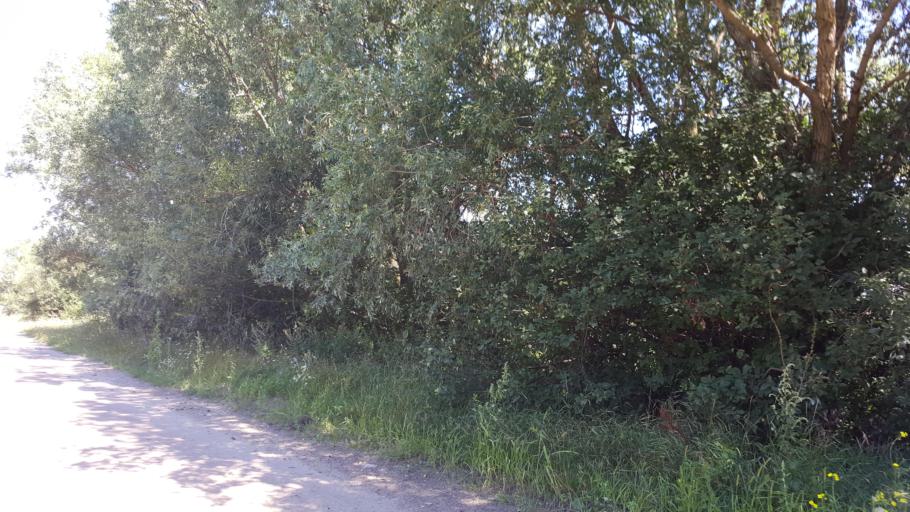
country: BY
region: Brest
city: Charnawchytsy
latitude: 52.2237
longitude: 23.7801
